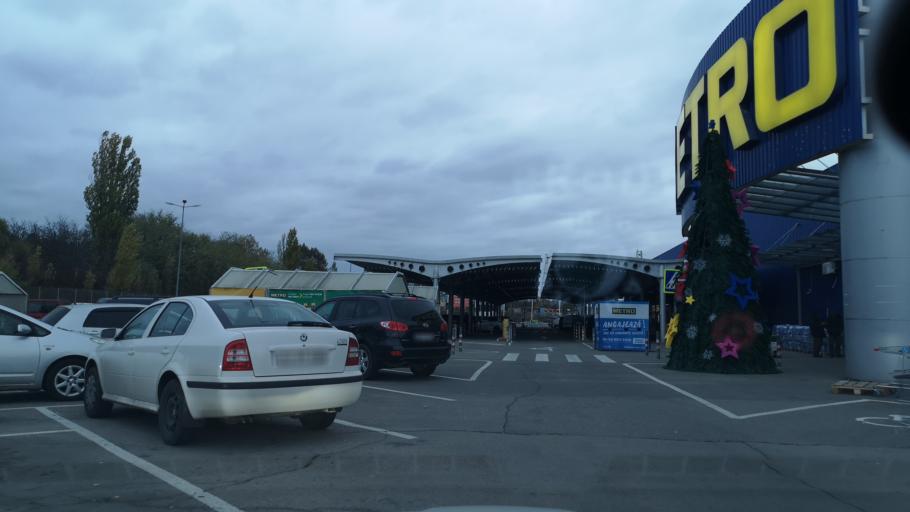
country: MD
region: Chisinau
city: Chisinau
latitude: 46.9658
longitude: 28.8901
